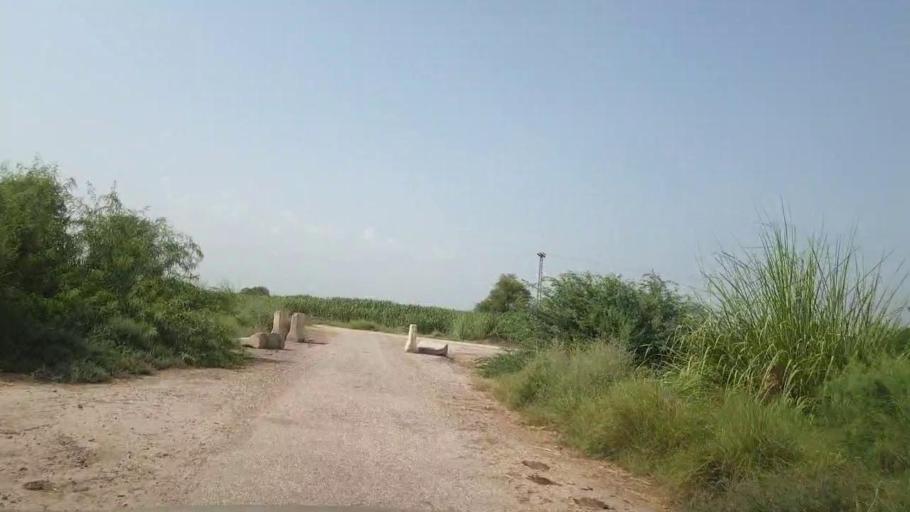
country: PK
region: Sindh
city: Pano Aqil
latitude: 27.7824
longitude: 69.1598
